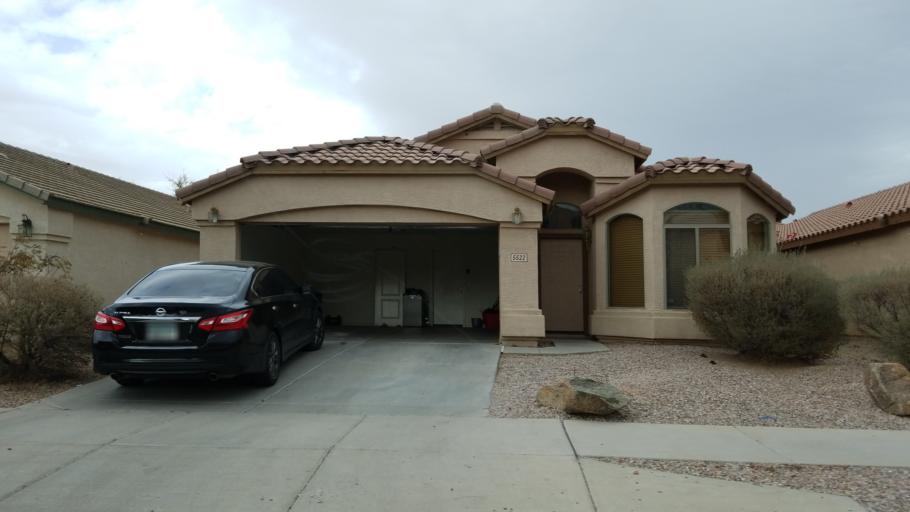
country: US
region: Arizona
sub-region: Maricopa County
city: Laveen
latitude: 33.4100
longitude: -112.1787
